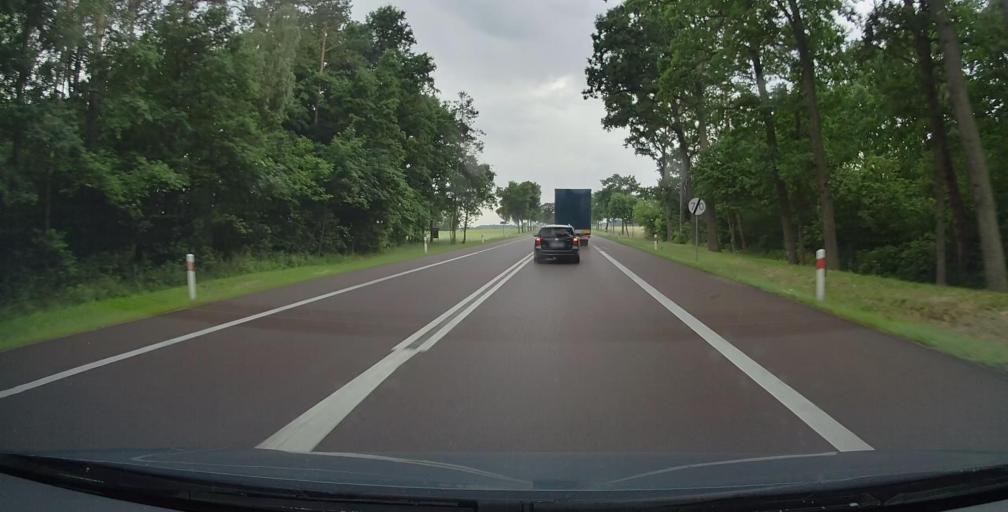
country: PL
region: Lublin Voivodeship
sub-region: Powiat bialski
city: Drelow
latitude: 52.0336
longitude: 22.9125
